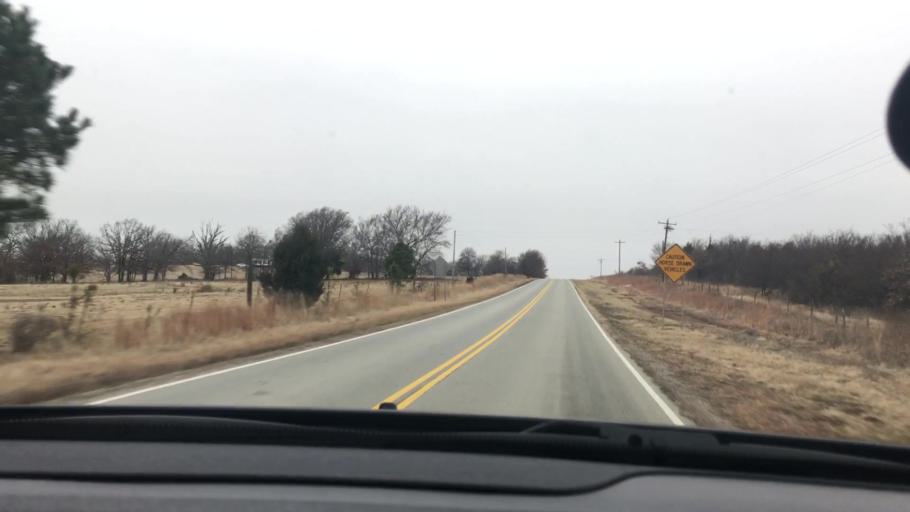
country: US
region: Oklahoma
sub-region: Coal County
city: Coalgate
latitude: 34.5055
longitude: -96.3440
